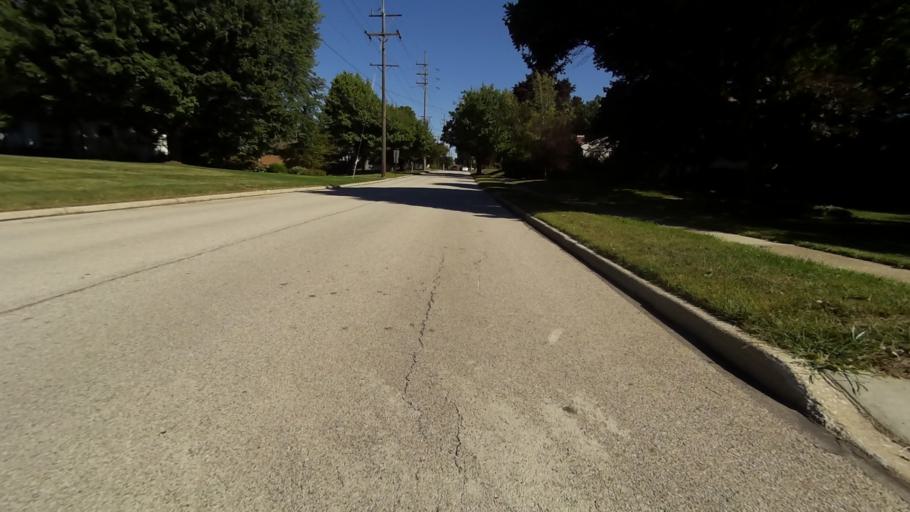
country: US
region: Ohio
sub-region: Portage County
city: Kent
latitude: 41.1460
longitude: -81.3775
